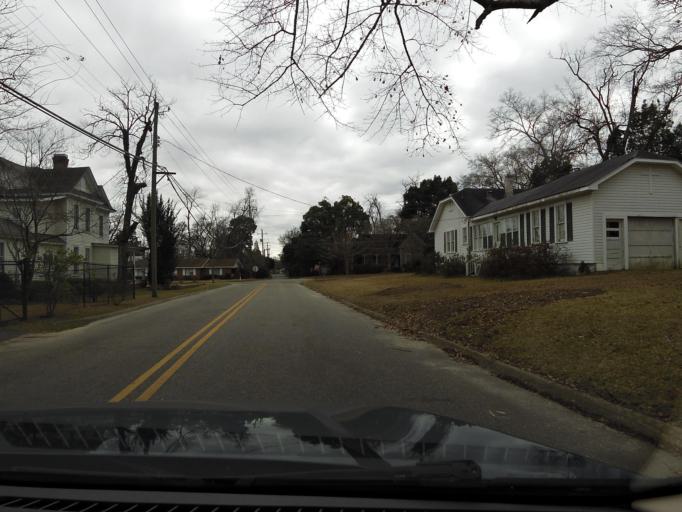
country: US
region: Alabama
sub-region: Barbour County
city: Eufaula
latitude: 31.8923
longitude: -85.1512
